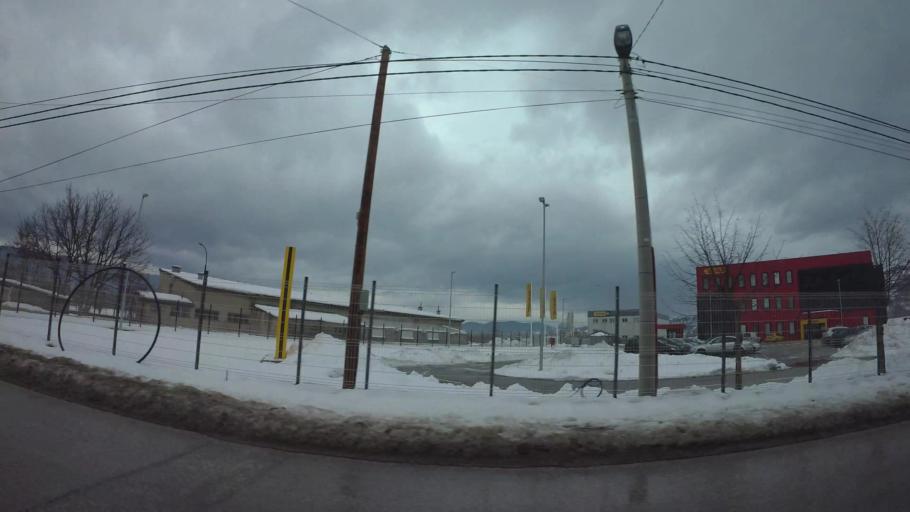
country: BA
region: Federation of Bosnia and Herzegovina
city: Vogosca
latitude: 43.8766
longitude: 18.3085
